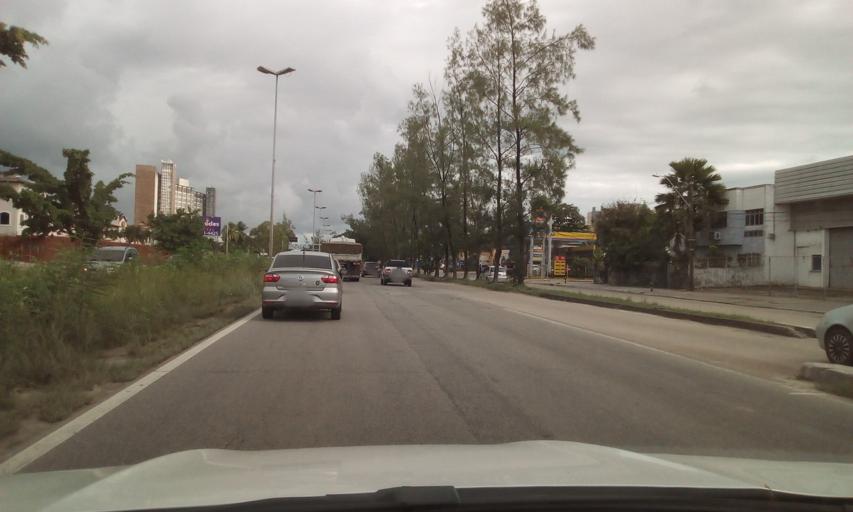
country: BR
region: Pernambuco
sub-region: Recife
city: Recife
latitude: -8.0436
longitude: -34.9438
